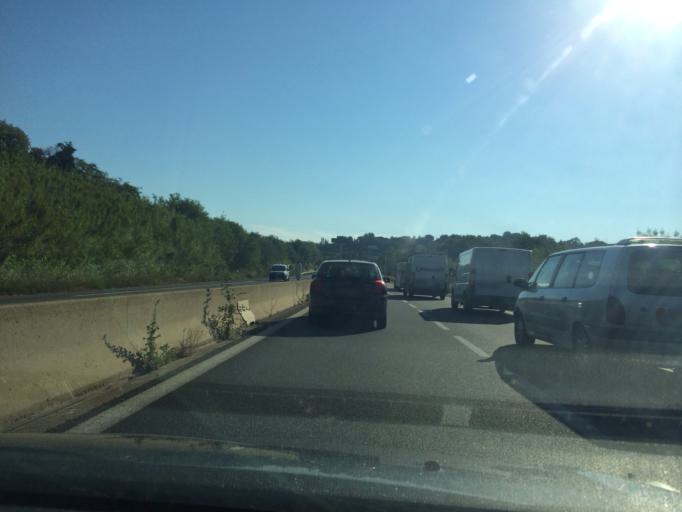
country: FR
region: Languedoc-Roussillon
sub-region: Departement de l'Herault
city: Juvignac
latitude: 43.6058
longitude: 3.8166
